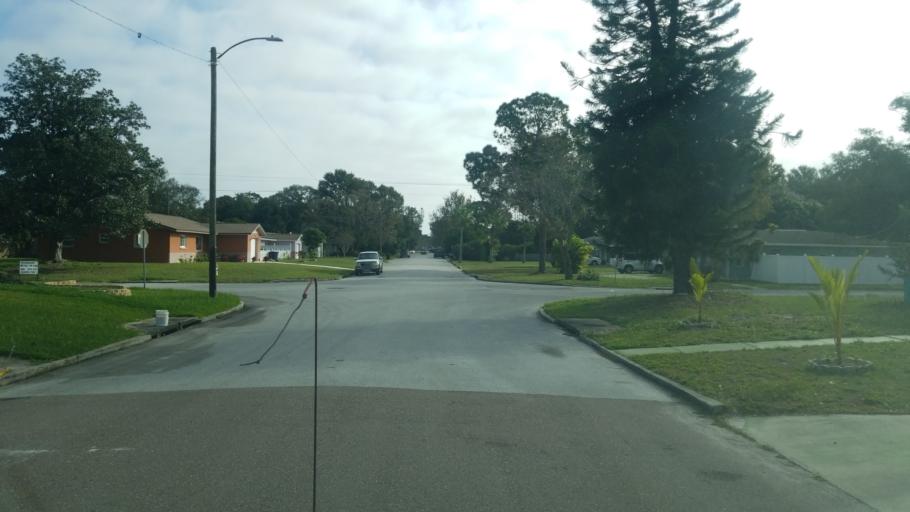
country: US
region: Florida
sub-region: Pinellas County
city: Saint Petersburg
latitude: 27.7956
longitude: -82.6738
